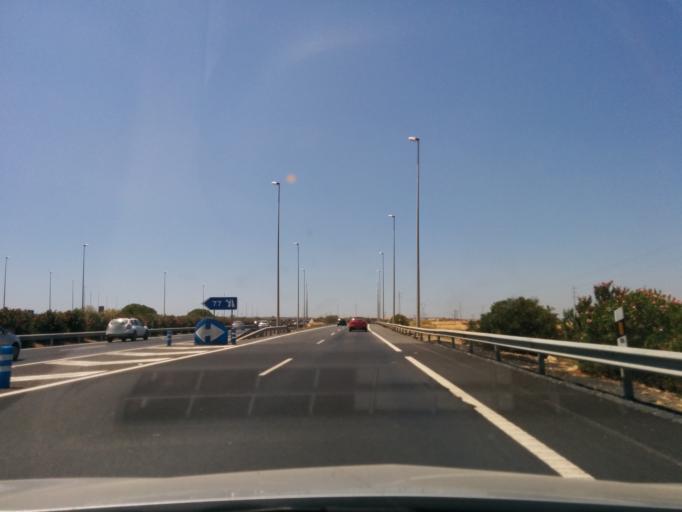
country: ES
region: Andalusia
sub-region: Provincia de Huelva
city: San Juan del Puerto
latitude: 37.3149
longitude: -6.8701
